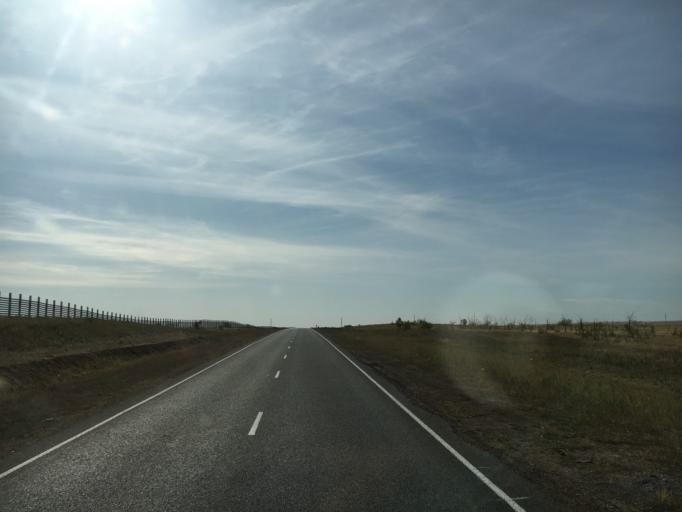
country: KZ
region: Batys Qazaqstan
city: Kamenka
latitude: 51.1090
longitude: 50.4466
